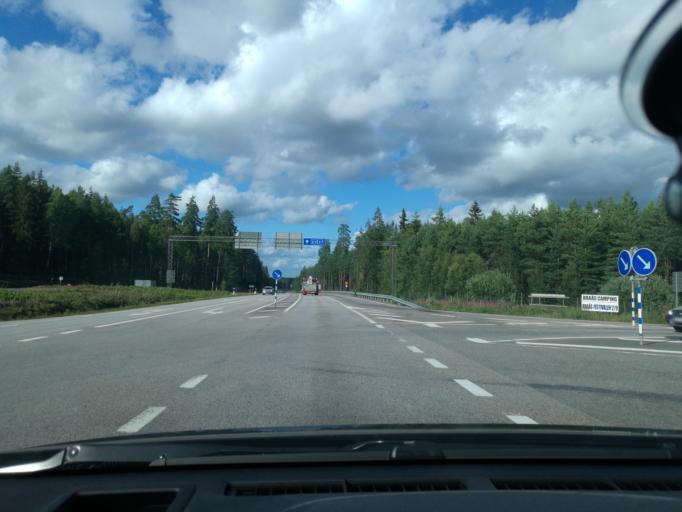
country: SE
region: Kronoberg
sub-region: Vaxjo Kommun
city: Braas
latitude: 57.0170
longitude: 15.0542
